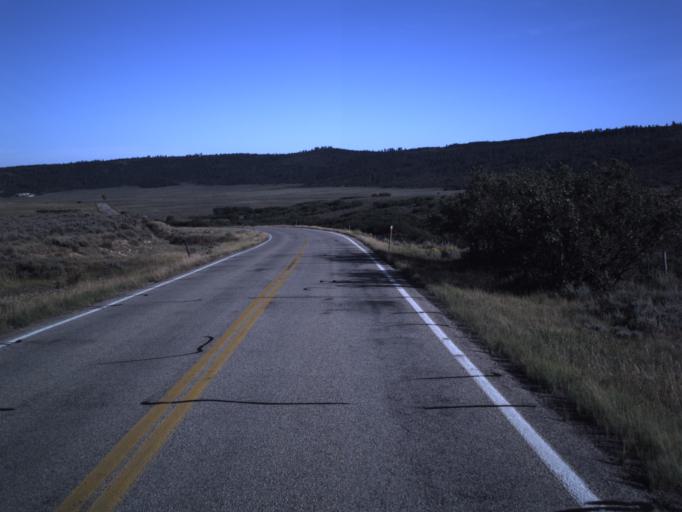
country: US
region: Utah
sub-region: Grand County
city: Moab
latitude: 38.3364
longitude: -109.1609
